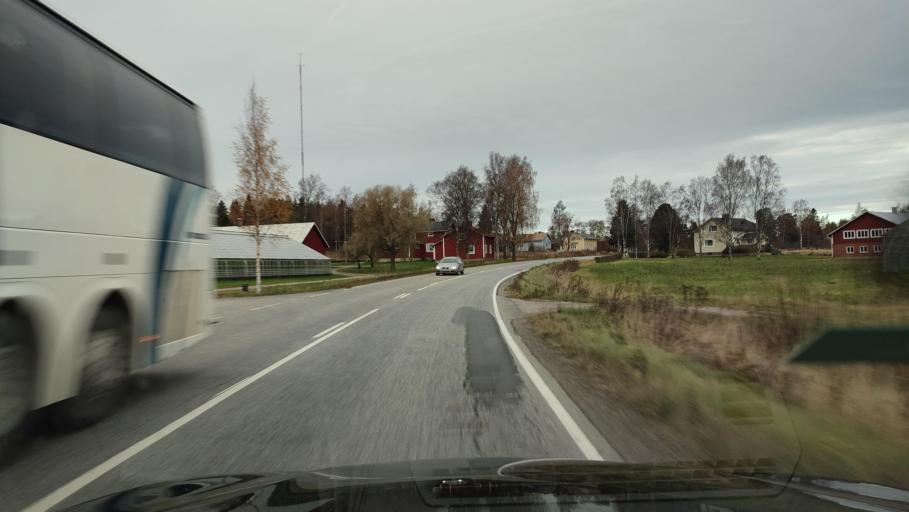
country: FI
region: Ostrobothnia
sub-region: Sydosterbotten
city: Naerpes
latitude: 62.4057
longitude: 21.3508
